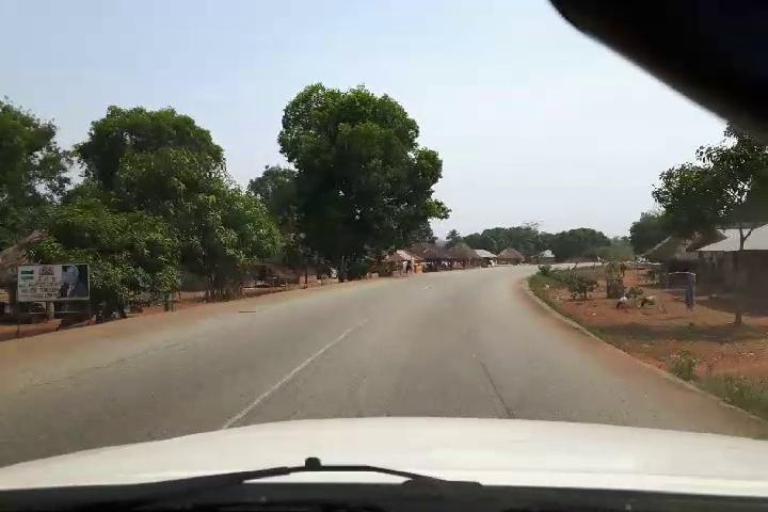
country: SL
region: Northern Province
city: Yonibana
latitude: 8.3985
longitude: -12.1947
